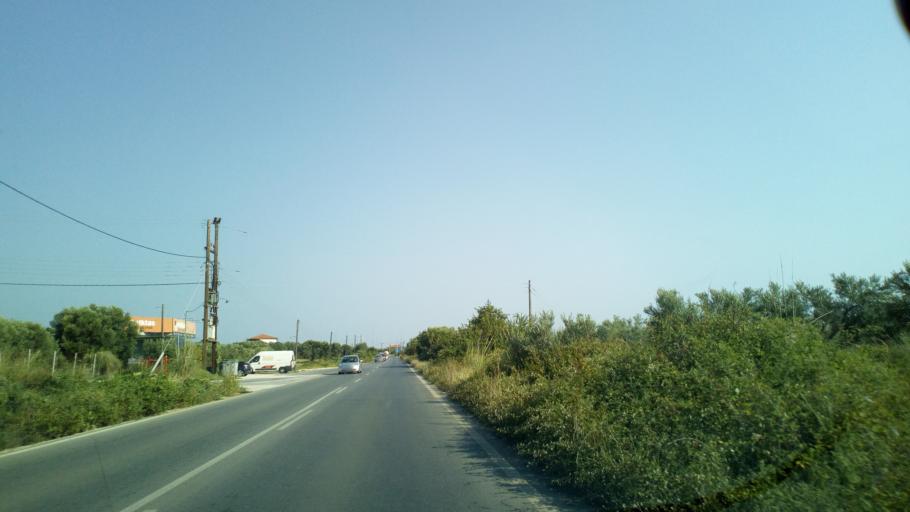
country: GR
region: Central Macedonia
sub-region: Nomos Chalkidikis
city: Kalyves Polygyrou
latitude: 40.2743
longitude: 23.4472
